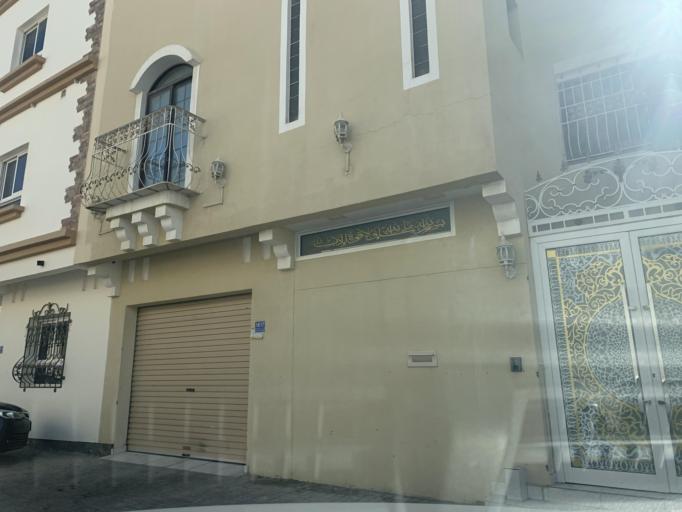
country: BH
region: Manama
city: Jidd Hafs
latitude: 26.2094
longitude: 50.5647
